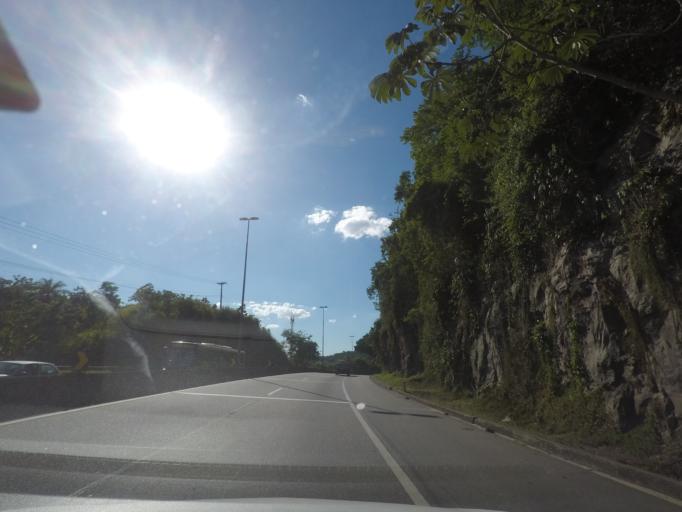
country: BR
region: Rio de Janeiro
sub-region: Petropolis
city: Petropolis
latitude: -22.6640
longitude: -43.1138
